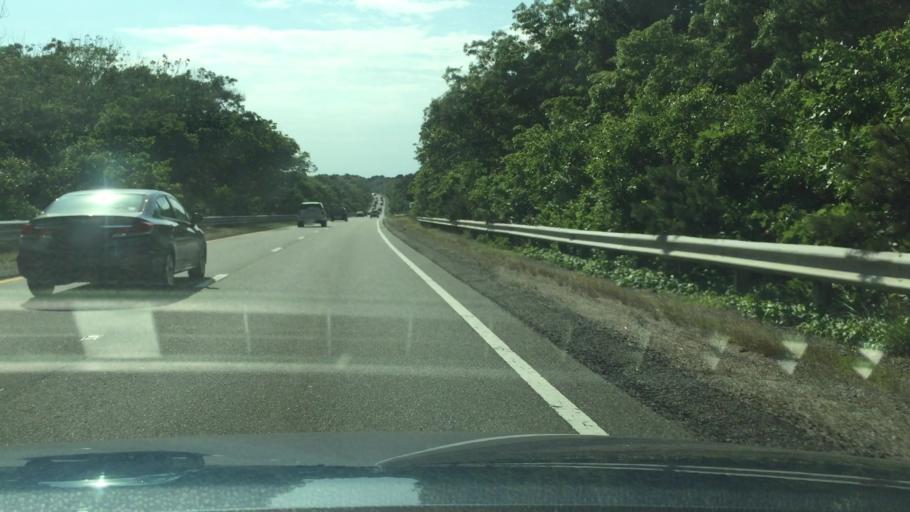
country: US
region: Massachusetts
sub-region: Barnstable County
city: Barnstable
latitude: 41.6881
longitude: -70.3040
